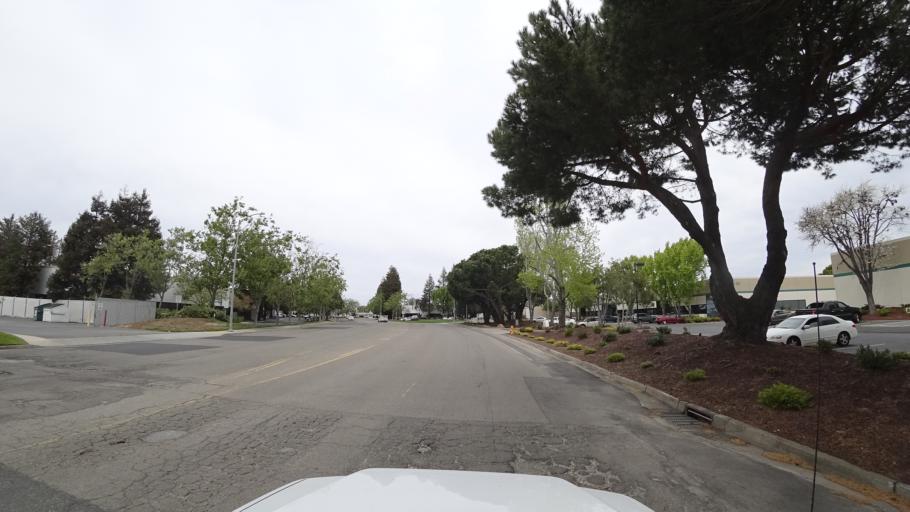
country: US
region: California
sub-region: Alameda County
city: San Lorenzo
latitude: 37.6497
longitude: -122.1376
